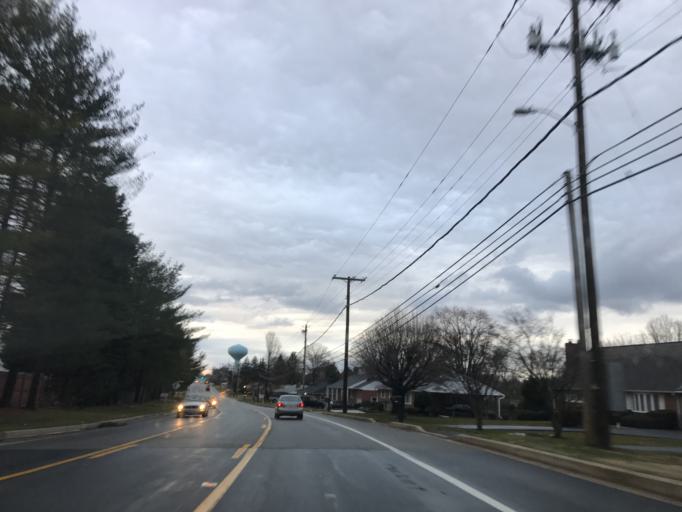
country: US
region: Maryland
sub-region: Harford County
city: Bel Air South
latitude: 39.5345
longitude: -76.2978
